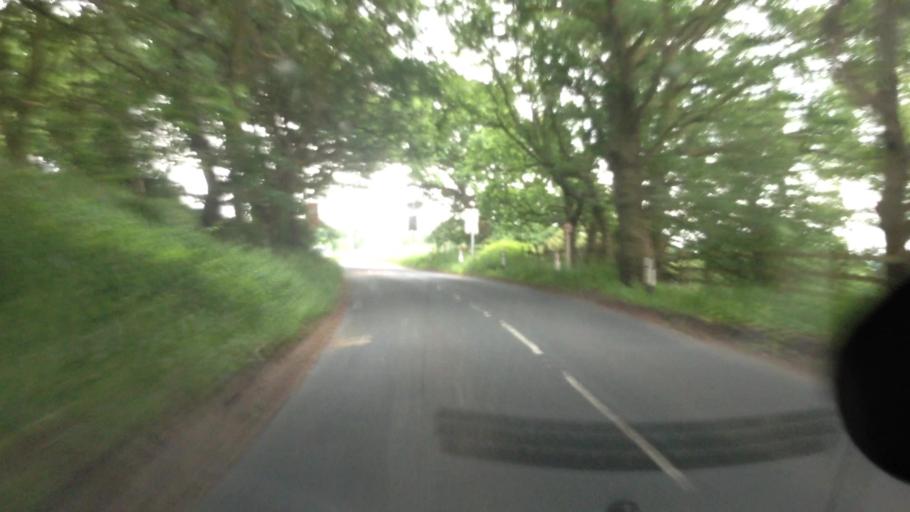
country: GB
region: England
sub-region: City and Borough of Wakefield
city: Woolley
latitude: 53.6155
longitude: -1.5377
